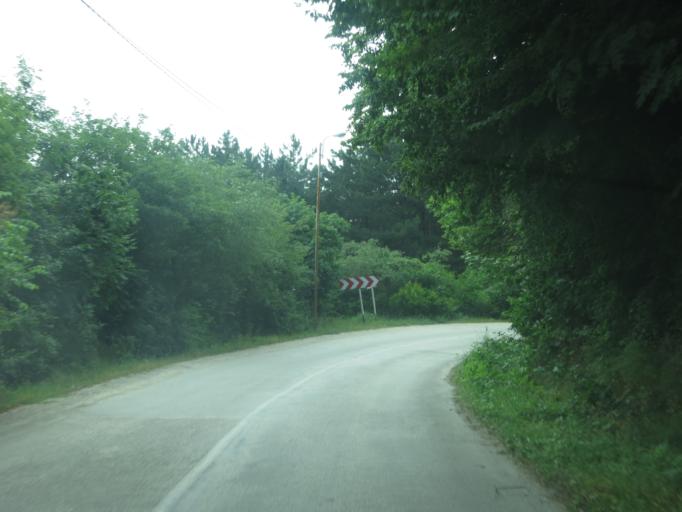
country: GE
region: Kakheti
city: Sighnaghi
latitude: 41.6106
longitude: 45.9242
